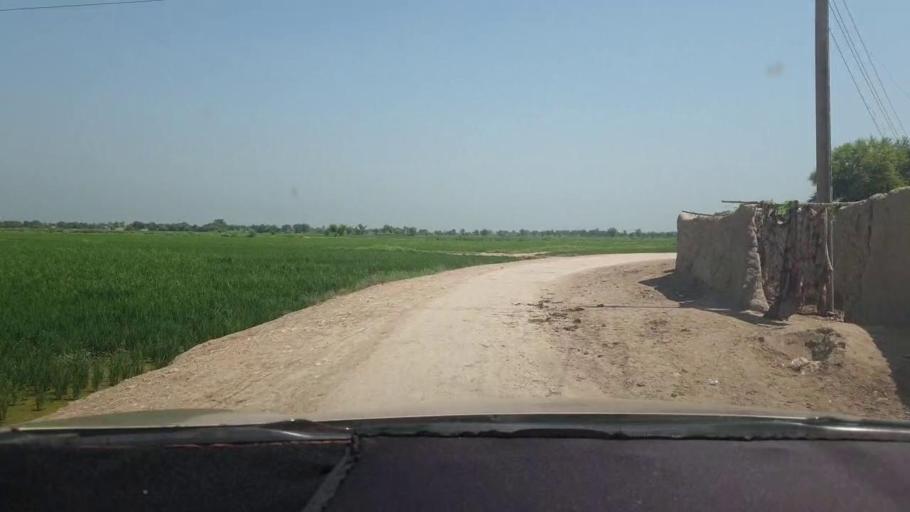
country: PK
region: Sindh
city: Miro Khan
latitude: 27.6698
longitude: 68.0990
